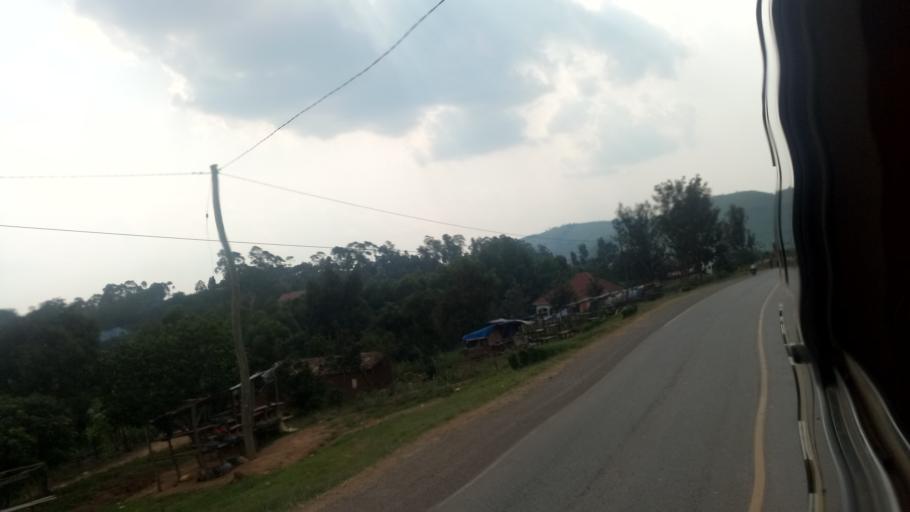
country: UG
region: Western Region
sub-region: Mbarara District
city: Mbarara
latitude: -0.5471
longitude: 30.7140
